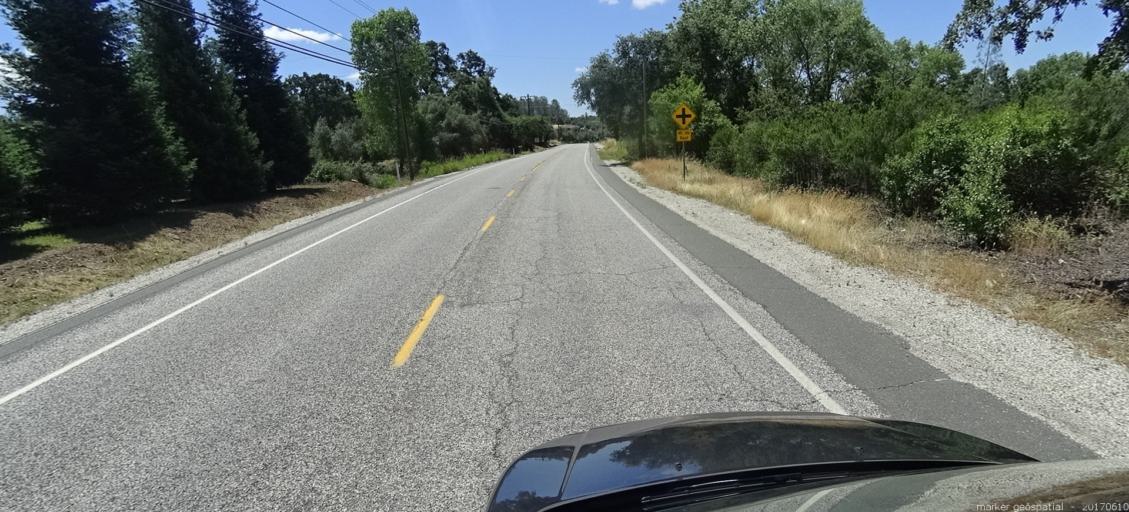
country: US
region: California
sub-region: Butte County
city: Oroville East
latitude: 39.4936
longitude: -121.4571
